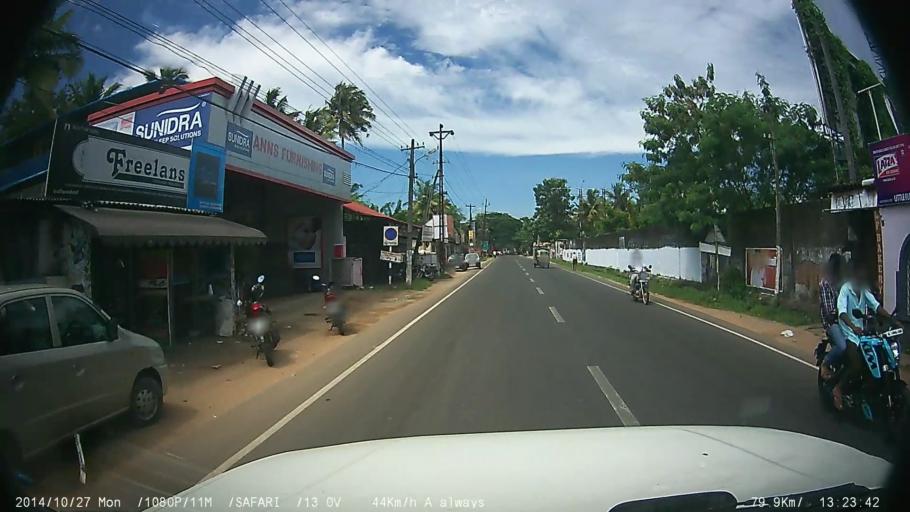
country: IN
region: Kerala
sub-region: Alappuzha
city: Alleppey
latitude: 9.5054
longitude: 76.3284
